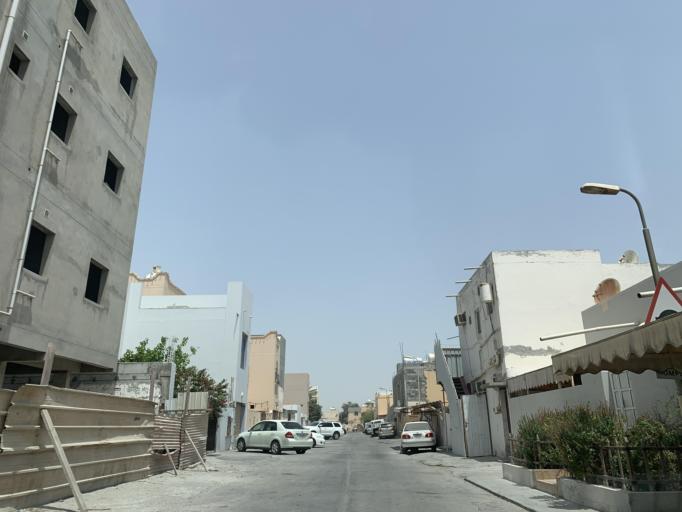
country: BH
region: Northern
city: Madinat `Isa
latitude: 26.1623
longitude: 50.5273
